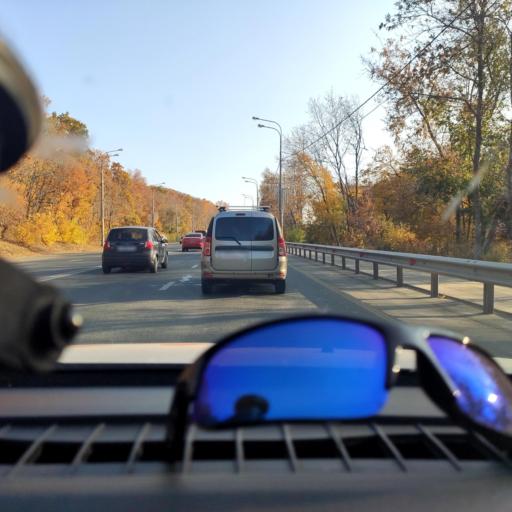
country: RU
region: Samara
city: Samara
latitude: 53.2844
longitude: 50.2272
